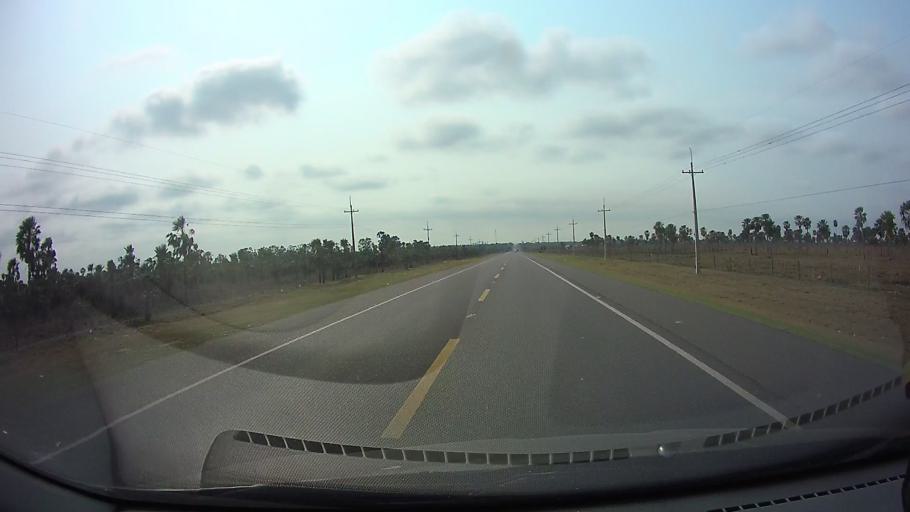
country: PY
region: Cordillera
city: Emboscada
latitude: -25.0696
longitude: -57.2410
